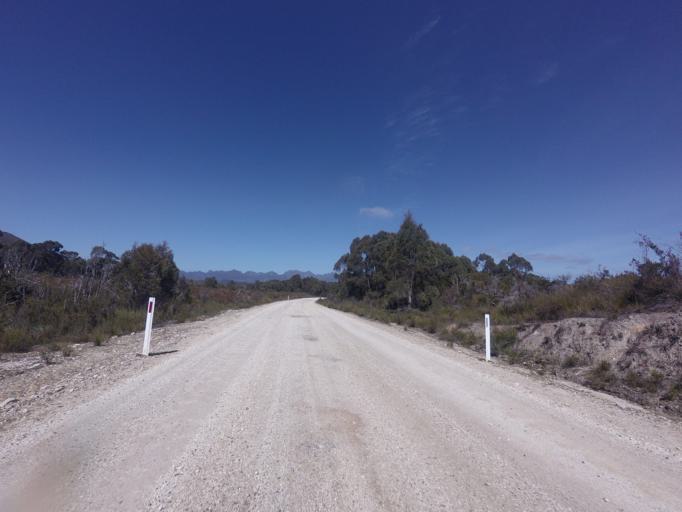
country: AU
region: Tasmania
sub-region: Huon Valley
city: Geeveston
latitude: -43.0258
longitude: 146.3543
